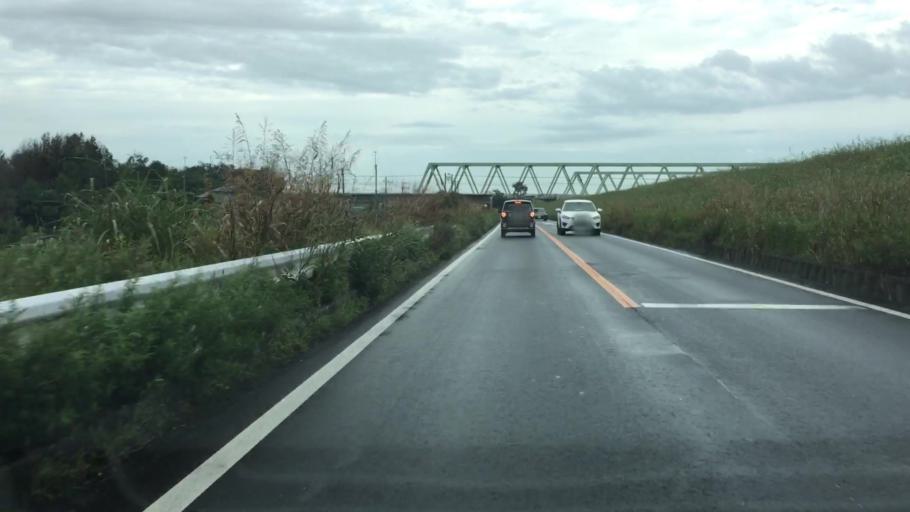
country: JP
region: Ibaraki
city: Toride
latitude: 35.8838
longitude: 140.0593
